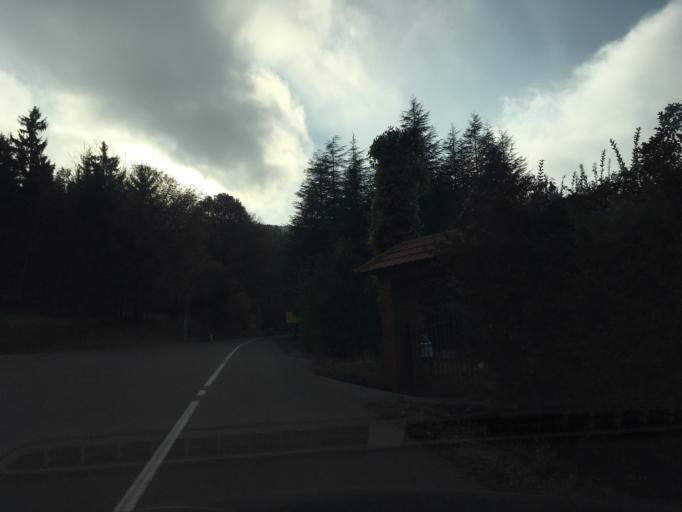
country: RS
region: Central Serbia
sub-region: Belgrade
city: Sopot
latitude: 44.4740
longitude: 20.5670
